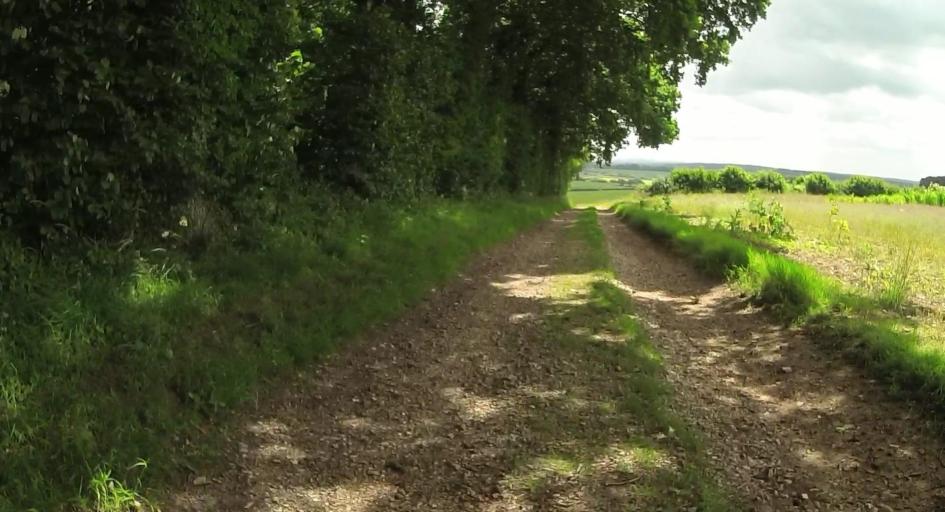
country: GB
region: England
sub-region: Hampshire
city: Basingstoke
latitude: 51.1789
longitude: -1.1649
